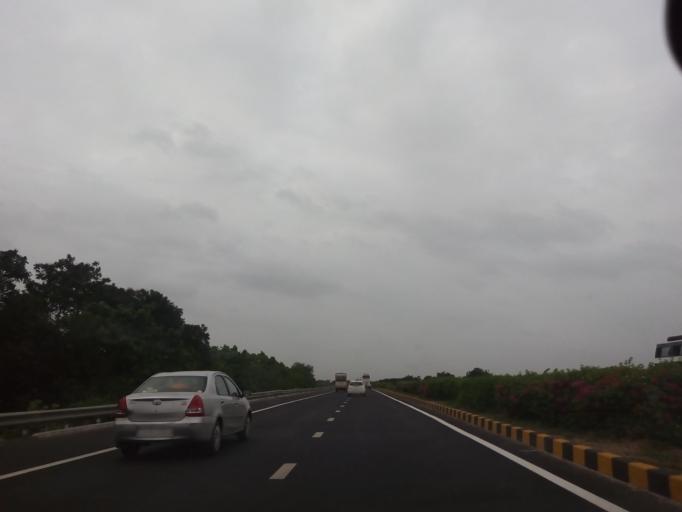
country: IN
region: Gujarat
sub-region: Kheda
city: Nadiad
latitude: 22.7379
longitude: 72.8650
